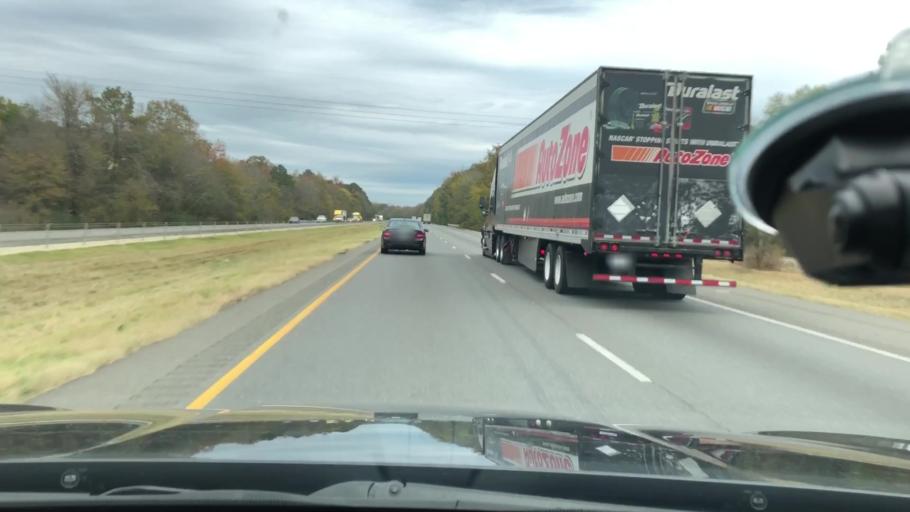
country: US
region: Arkansas
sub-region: Hot Spring County
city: Malvern
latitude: 34.3645
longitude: -92.8694
